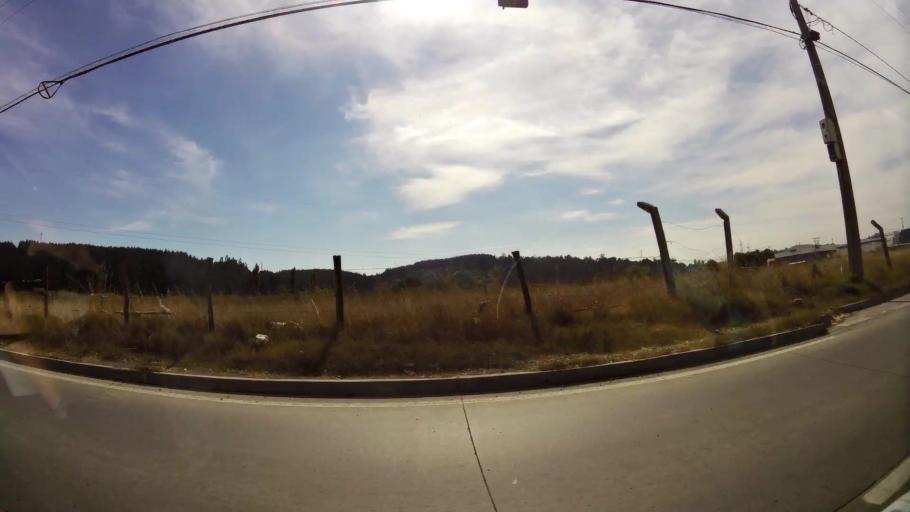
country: CL
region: Biobio
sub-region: Provincia de Concepcion
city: Talcahuano
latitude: -36.7623
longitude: -73.1179
